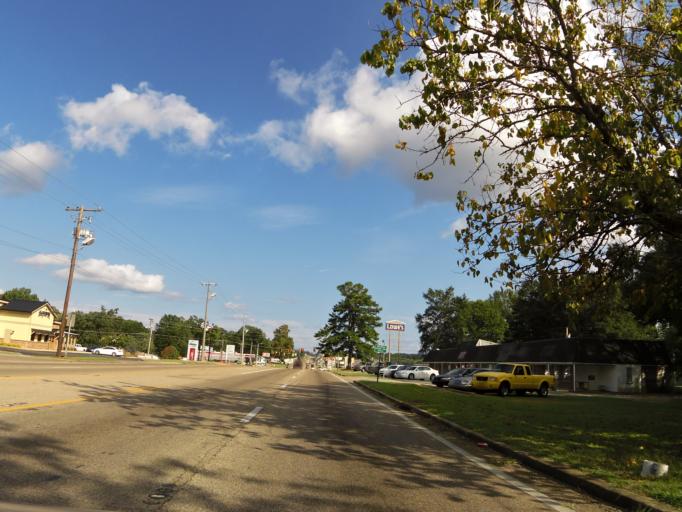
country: US
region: Mississippi
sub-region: Alcorn County
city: Corinth
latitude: 34.9170
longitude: -88.5074
